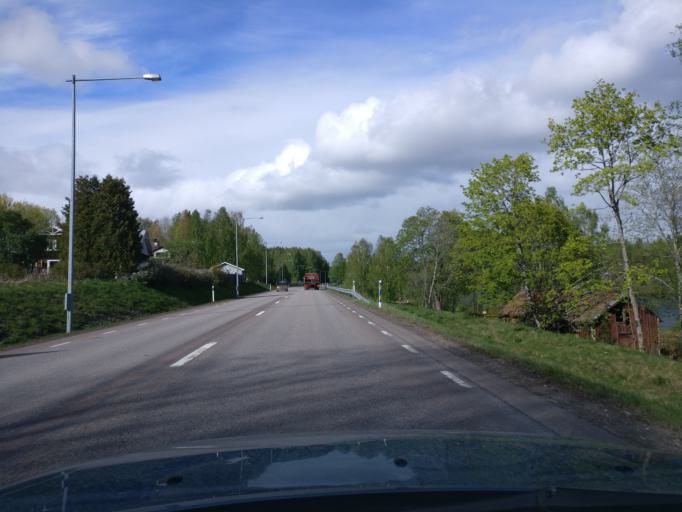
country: SE
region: Vaermland
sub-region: Forshaga Kommun
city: Forshaga
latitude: 59.5145
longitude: 13.4419
